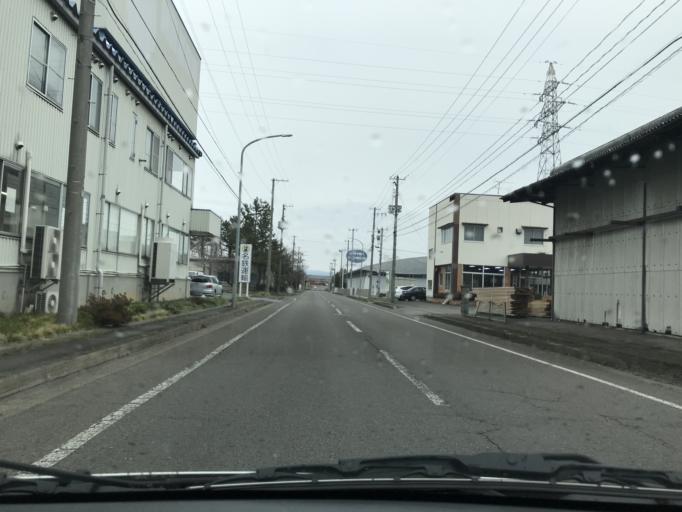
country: JP
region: Iwate
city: Mizusawa
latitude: 39.1796
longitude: 141.1146
